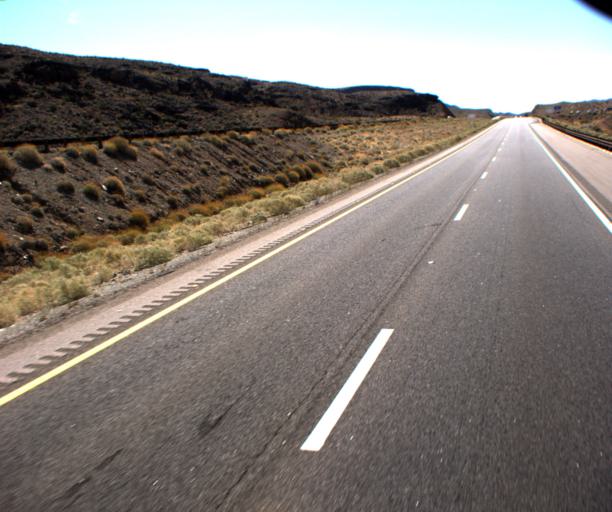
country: US
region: Nevada
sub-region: Clark County
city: Boulder City
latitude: 35.8858
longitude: -114.6194
